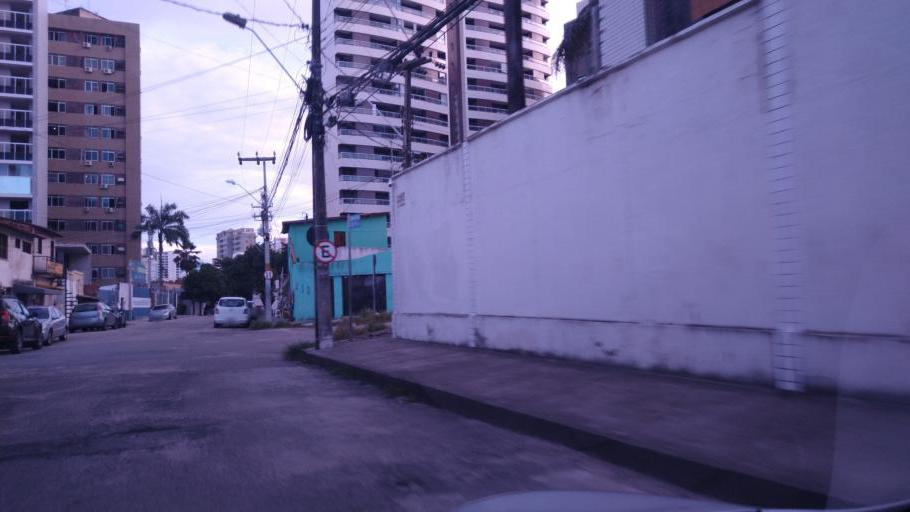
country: BR
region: Ceara
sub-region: Fortaleza
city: Fortaleza
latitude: -3.7278
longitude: -38.4880
